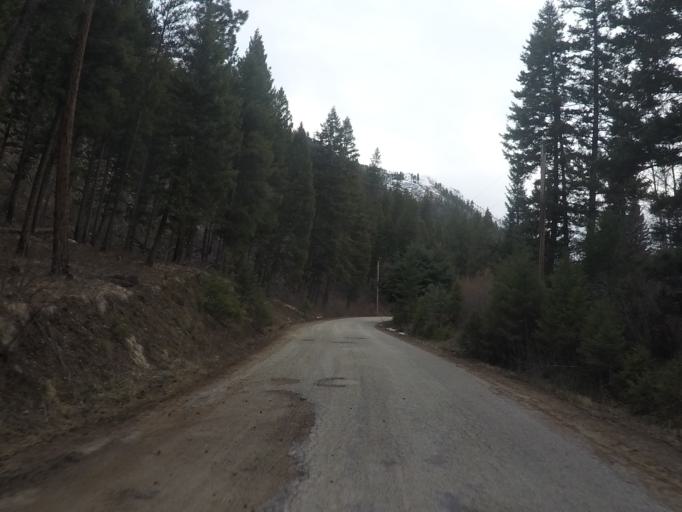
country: US
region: Montana
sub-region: Ravalli County
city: Hamilton
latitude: 45.8482
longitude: -114.0340
